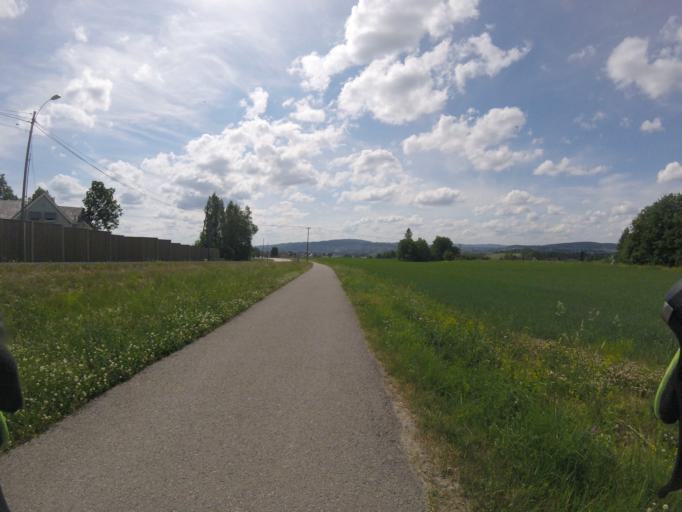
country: NO
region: Akershus
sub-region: Skedsmo
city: Lillestrom
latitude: 59.9881
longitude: 11.0477
